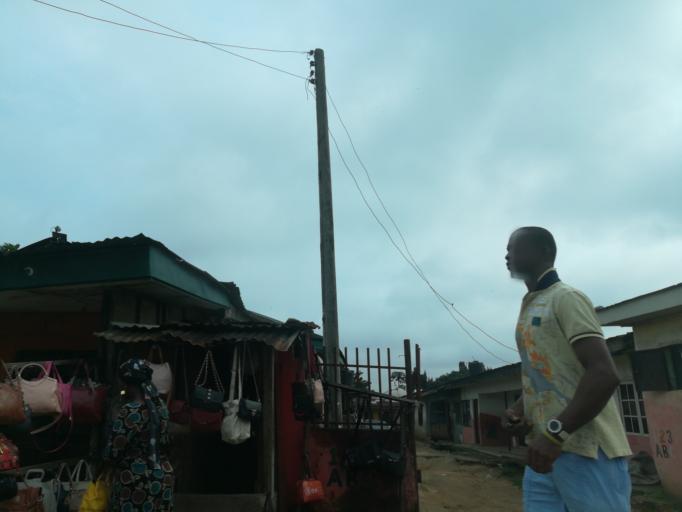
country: NG
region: Rivers
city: Port Harcourt
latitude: 4.8735
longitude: 6.9889
